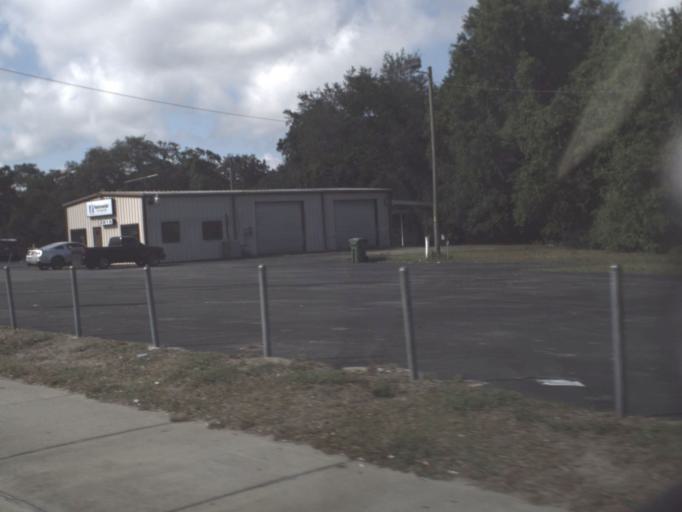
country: US
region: Florida
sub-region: Lake County
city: Fruitland Park
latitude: 28.8394
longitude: -81.8932
